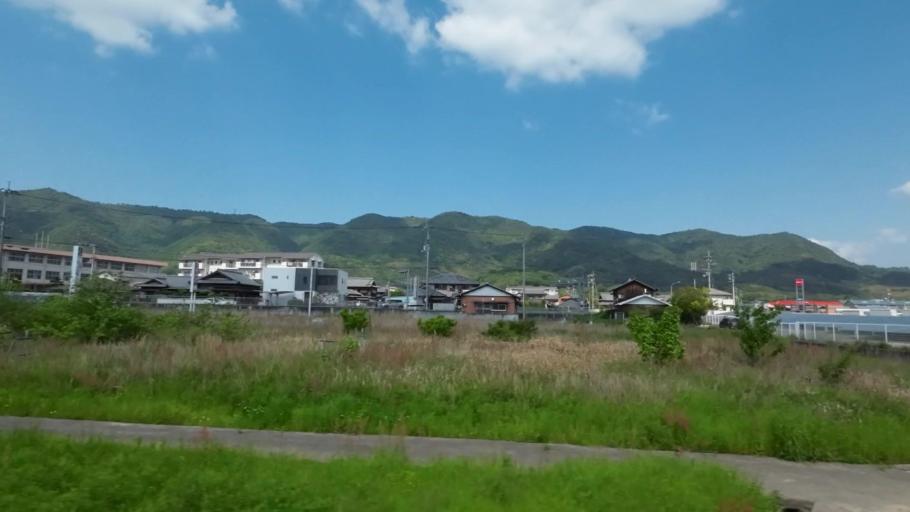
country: JP
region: Kagawa
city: Kan'onjicho
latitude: 34.1686
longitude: 133.6907
